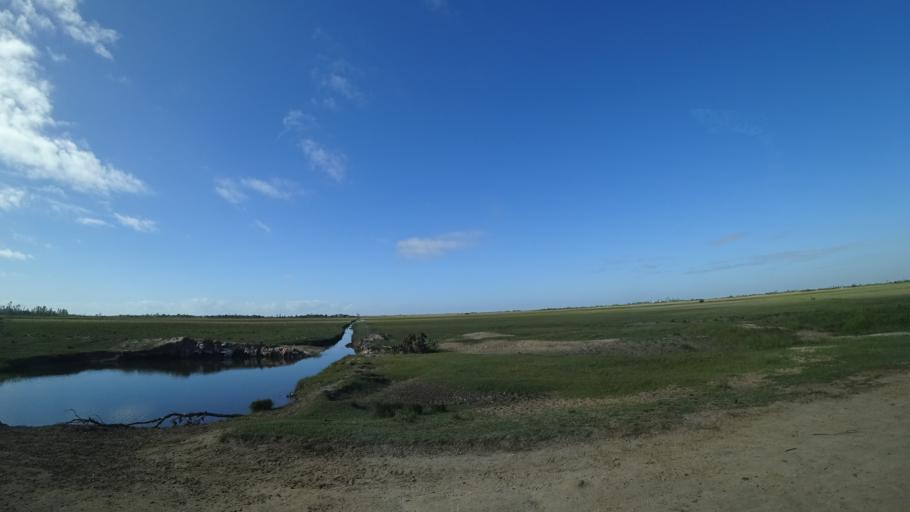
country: MZ
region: Sofala
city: Beira
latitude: -19.7272
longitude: 34.9884
